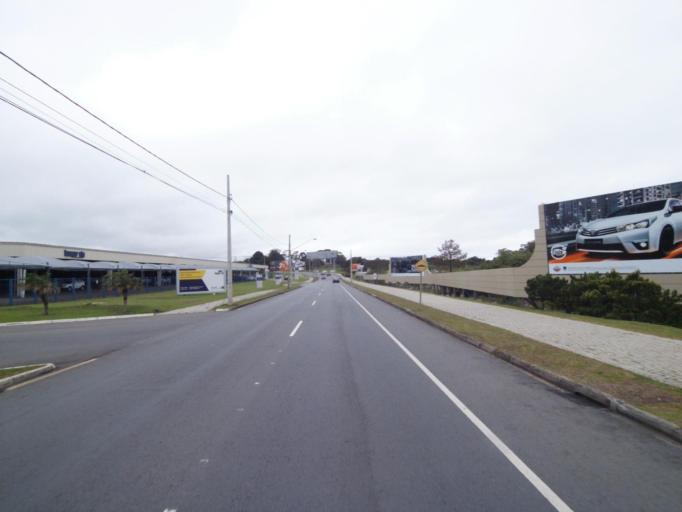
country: BR
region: Parana
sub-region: Sao Jose Dos Pinhais
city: Sao Jose dos Pinhais
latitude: -25.5372
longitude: -49.1845
